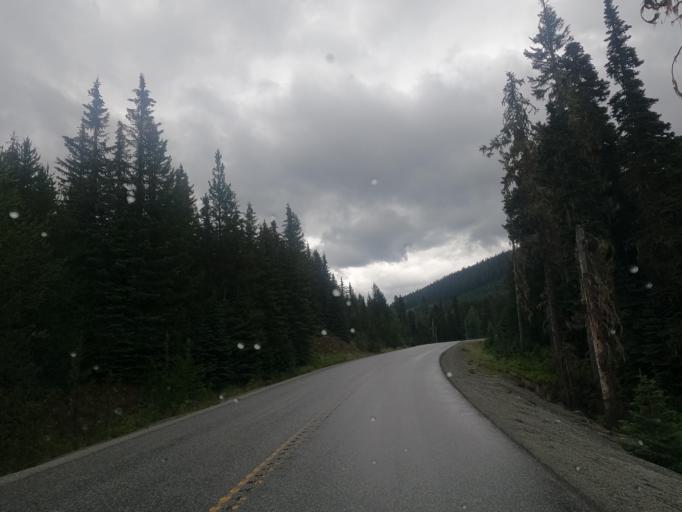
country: CA
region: British Columbia
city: Pemberton
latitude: 50.3803
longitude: -122.4766
